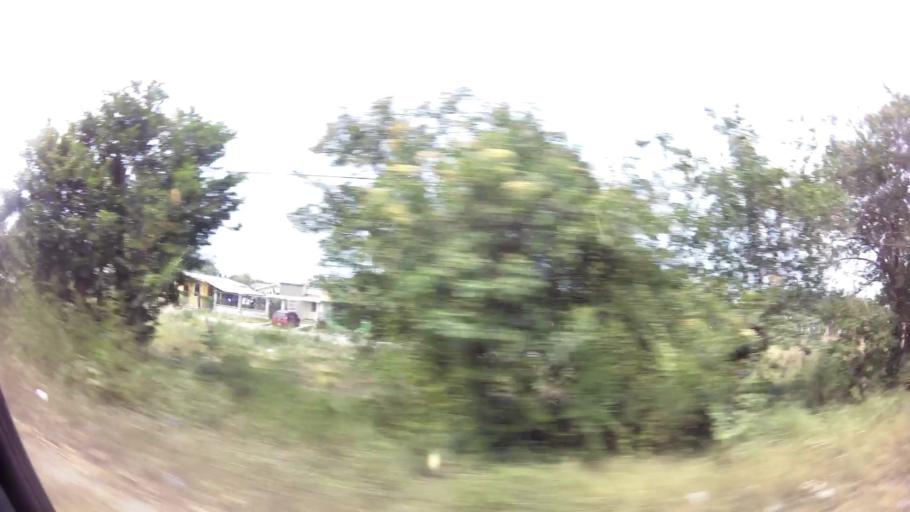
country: HN
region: Cortes
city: La Lima
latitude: 15.4279
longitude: -87.9001
